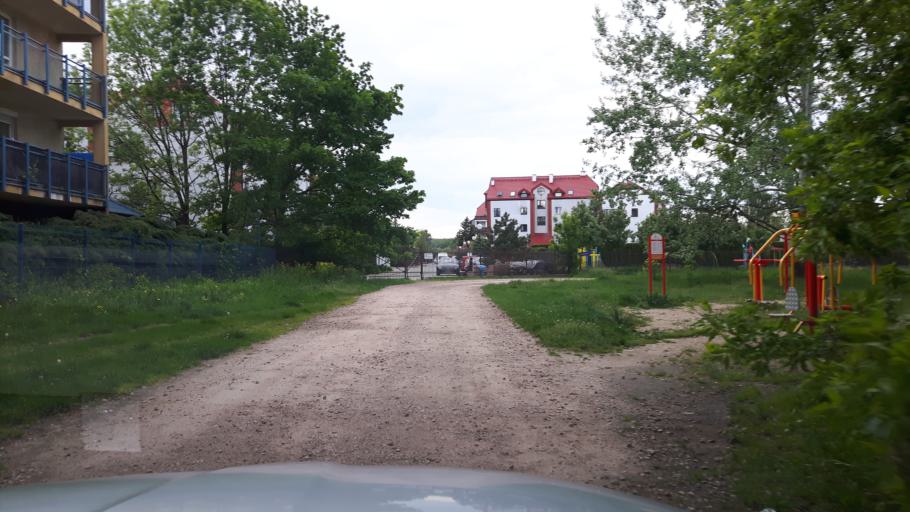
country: PL
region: Masovian Voivodeship
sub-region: Powiat wolominski
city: Zabki
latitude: 52.2892
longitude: 21.0843
